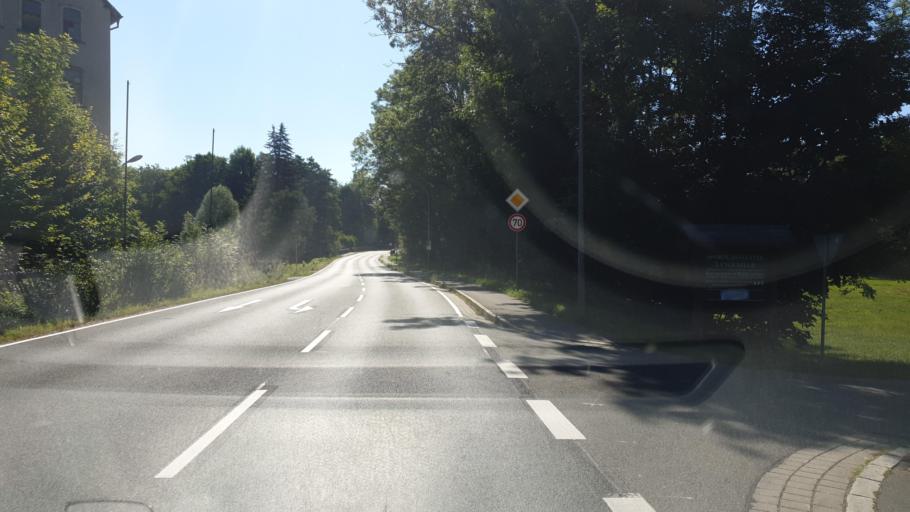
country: DE
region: Saxony
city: Lengenfeld
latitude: 50.5792
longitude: 12.3689
